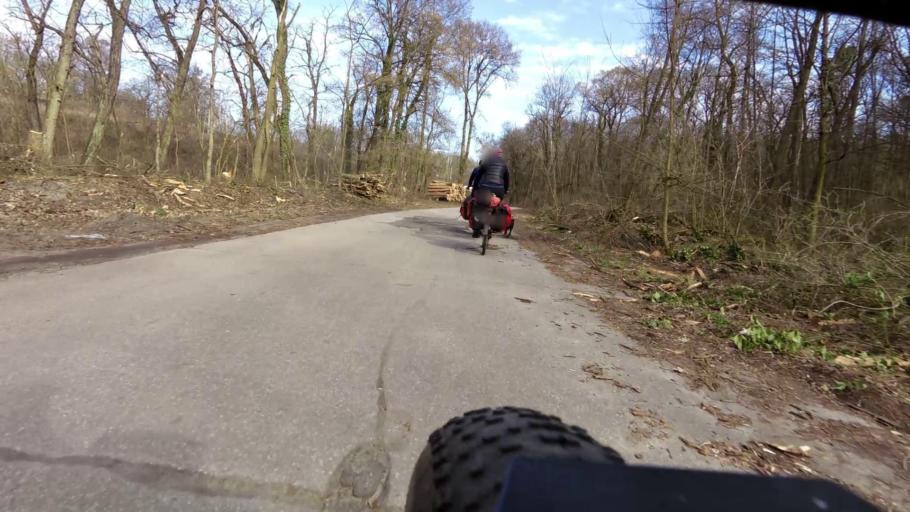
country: PL
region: Lubusz
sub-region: Powiat slubicki
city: Slubice
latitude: 52.3236
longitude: 14.5823
